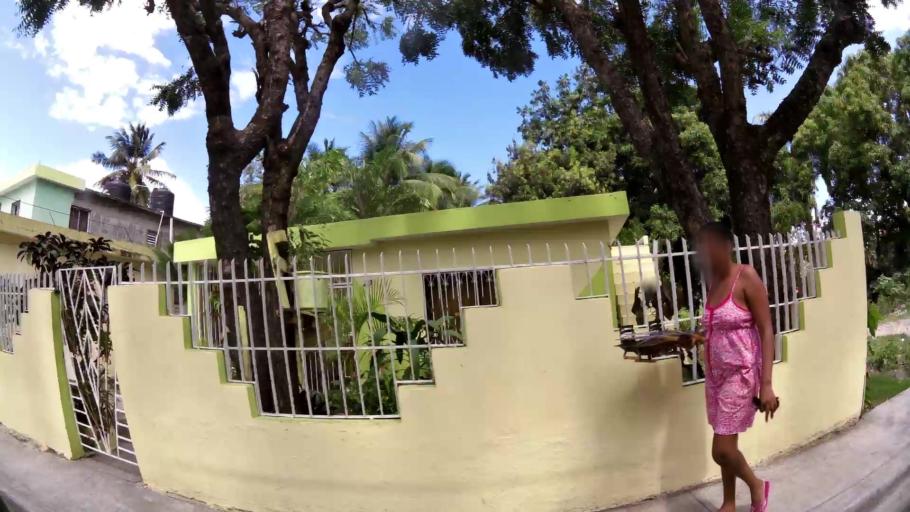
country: DO
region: San Cristobal
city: San Cristobal
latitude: 18.4229
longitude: -70.0950
